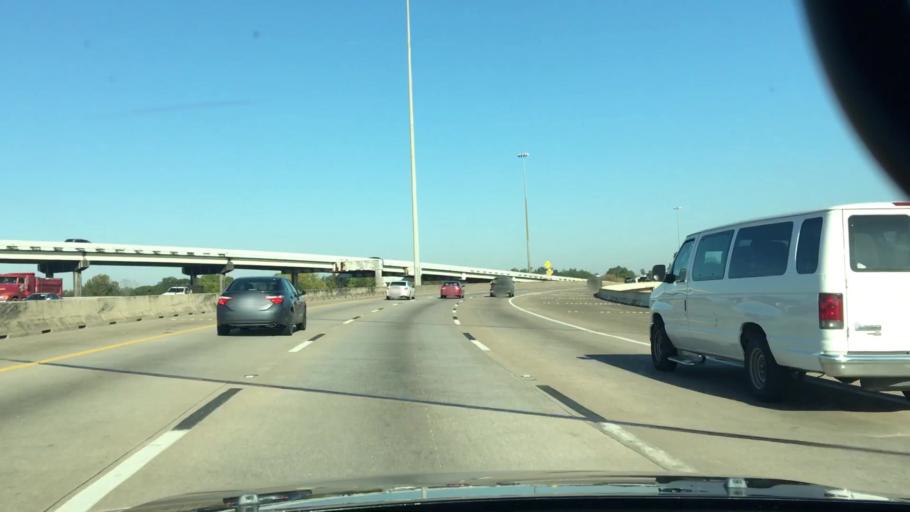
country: US
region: Texas
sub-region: Harris County
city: Bellaire
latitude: 29.6808
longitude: -95.4580
